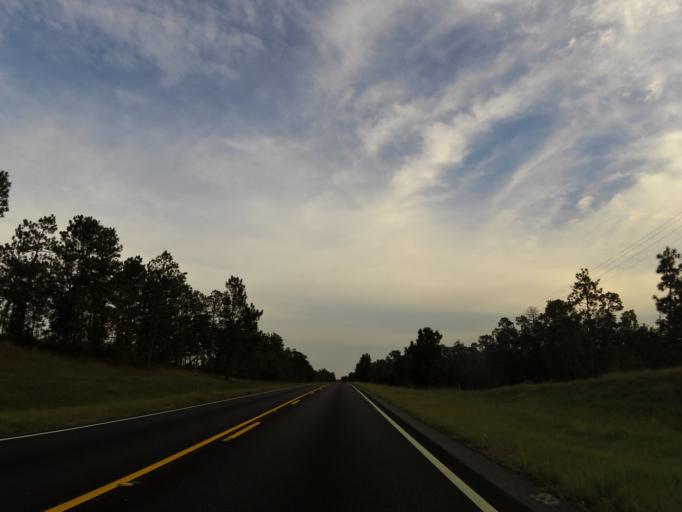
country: US
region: Alabama
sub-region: Monroe County
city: Frisco City
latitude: 31.2462
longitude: -87.4897
